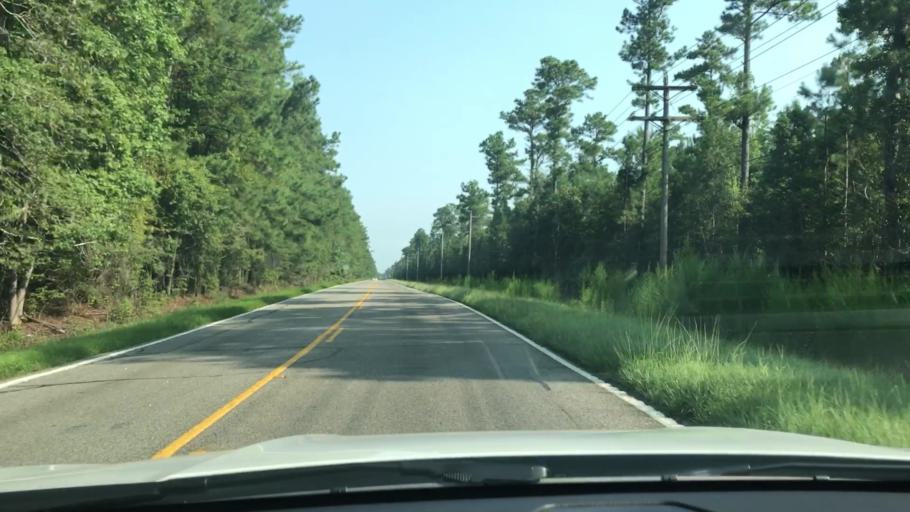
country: US
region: South Carolina
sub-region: Georgetown County
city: Georgetown
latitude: 33.4386
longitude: -79.2763
